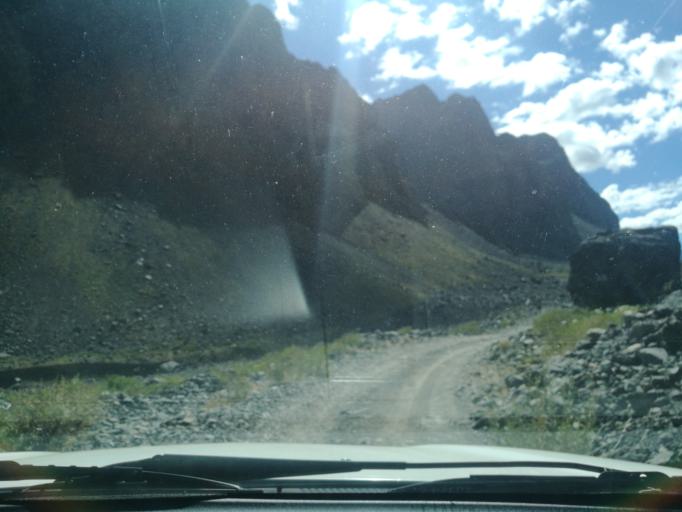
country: CL
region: O'Higgins
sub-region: Provincia de Cachapoal
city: Machali
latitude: -34.4048
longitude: -70.2484
